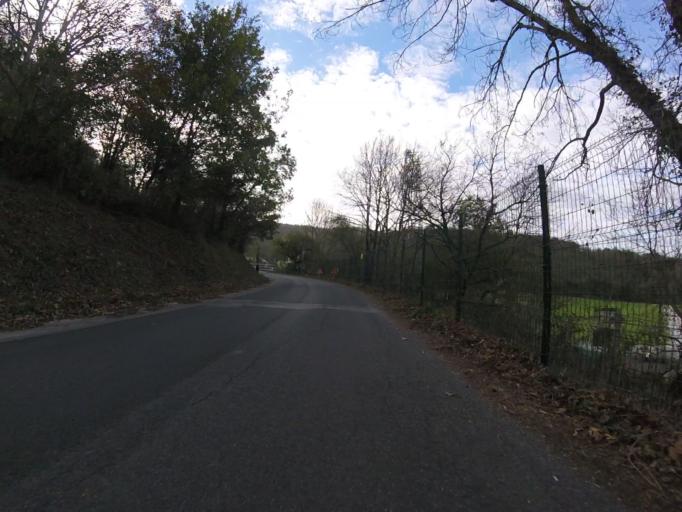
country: ES
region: Basque Country
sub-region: Provincia de Guipuzcoa
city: Errenteria
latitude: 43.3012
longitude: -1.9230
